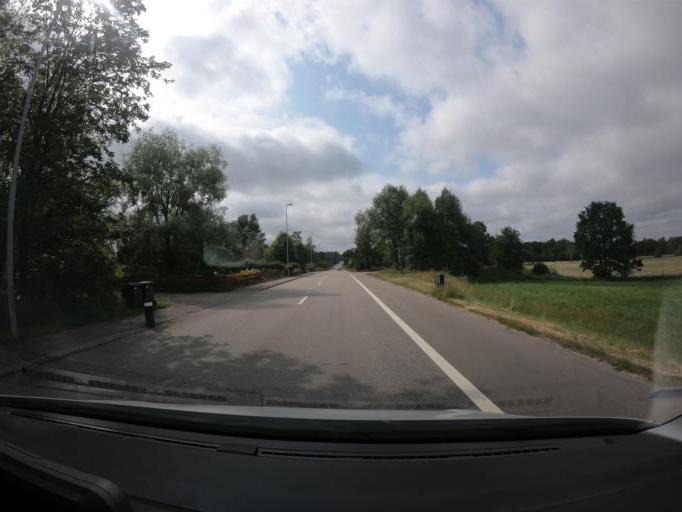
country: SE
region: Skane
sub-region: Perstorps Kommun
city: Perstorp
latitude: 56.2356
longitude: 13.5183
